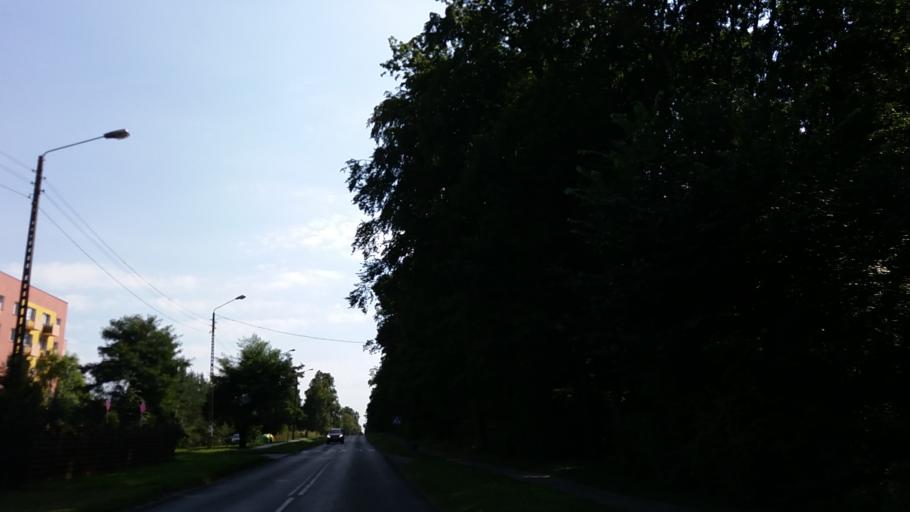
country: PL
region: West Pomeranian Voivodeship
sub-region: Powiat choszczenski
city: Choszczno
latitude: 53.1606
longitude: 15.4311
